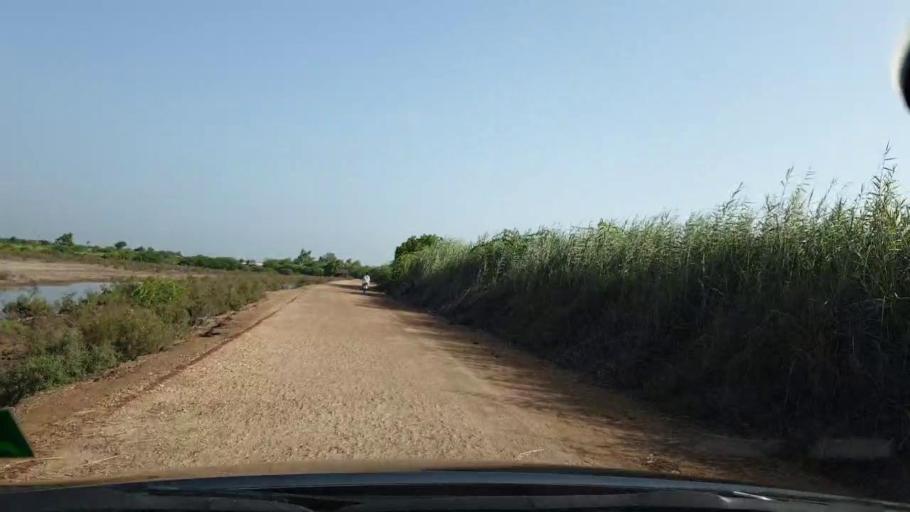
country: PK
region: Sindh
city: Tando Bago
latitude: 24.6561
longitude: 69.0416
